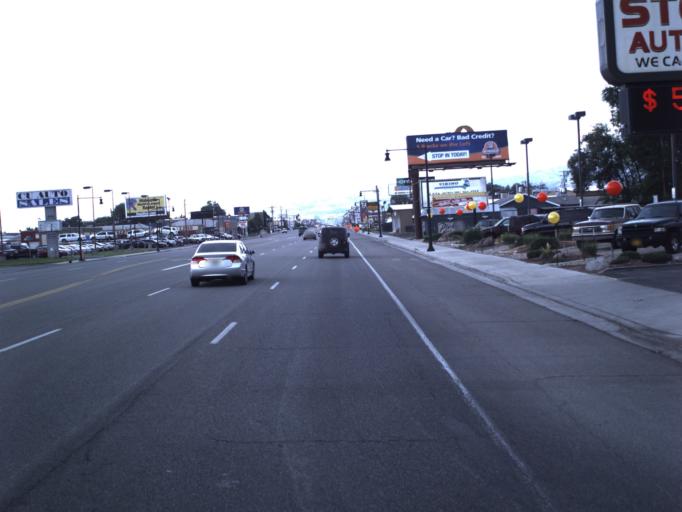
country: US
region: Utah
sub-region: Salt Lake County
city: Murray
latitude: 40.6804
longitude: -111.8882
